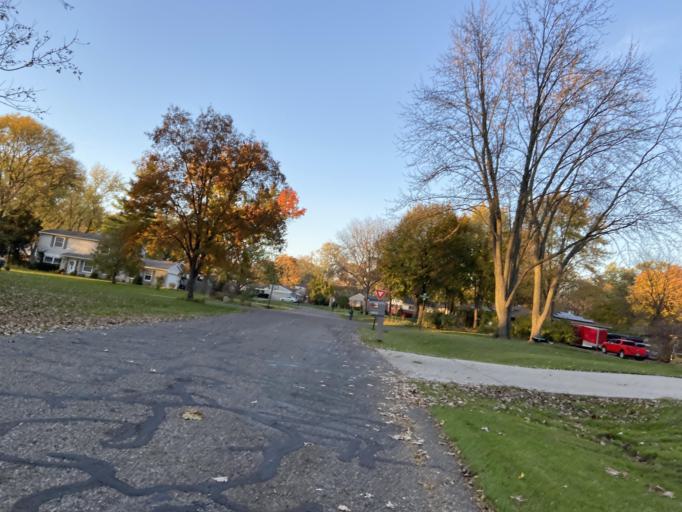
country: US
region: Michigan
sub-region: Oakland County
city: Farmington Hills
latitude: 42.5031
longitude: -83.3664
